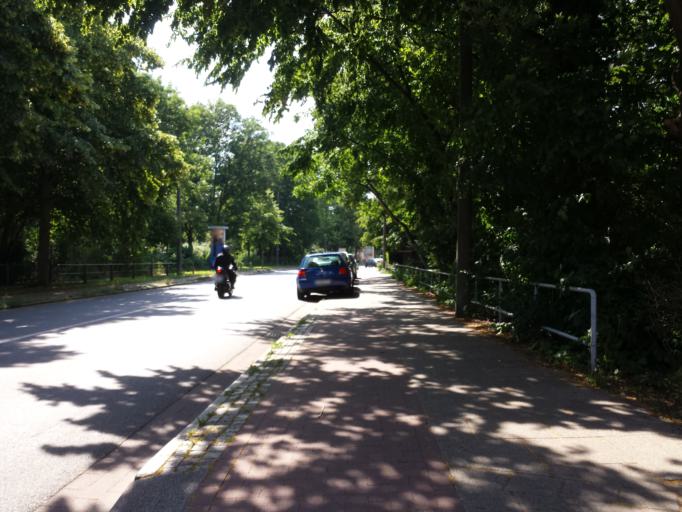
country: DE
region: Bremen
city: Bremen
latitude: 53.0883
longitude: 8.7580
